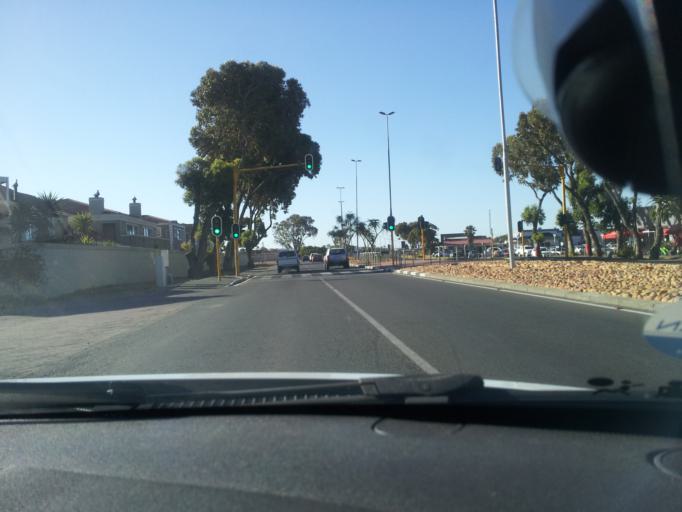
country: ZA
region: Western Cape
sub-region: Overberg District Municipality
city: Grabouw
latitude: -34.1476
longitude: 18.8570
